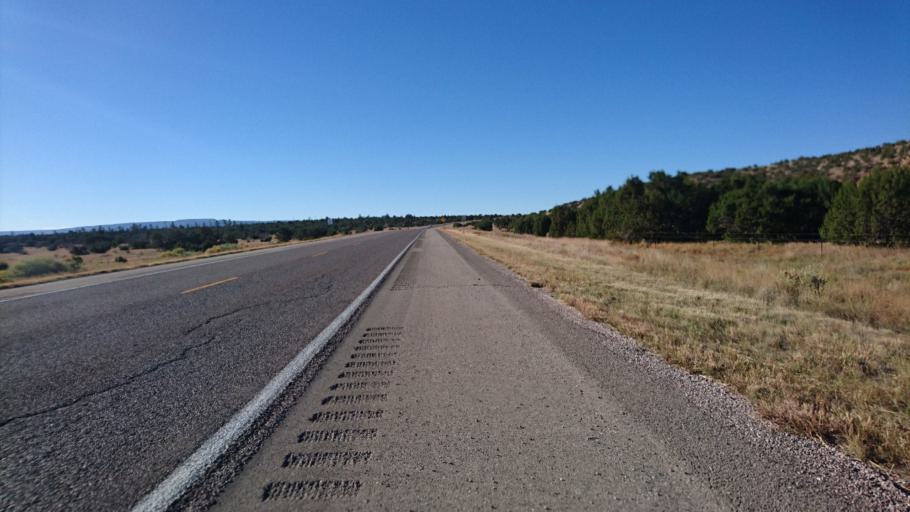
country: US
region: New Mexico
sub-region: Cibola County
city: Grants
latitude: 34.9697
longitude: -107.9127
